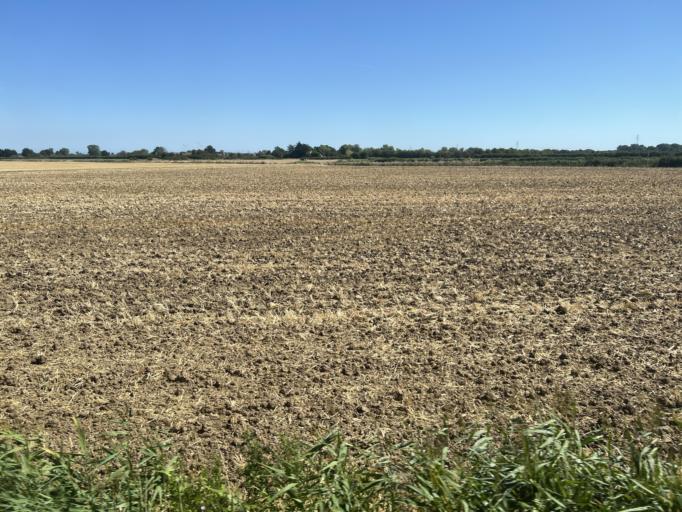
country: GB
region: England
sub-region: Lincolnshire
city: Wainfleet All Saints
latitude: 53.1251
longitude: 0.1976
